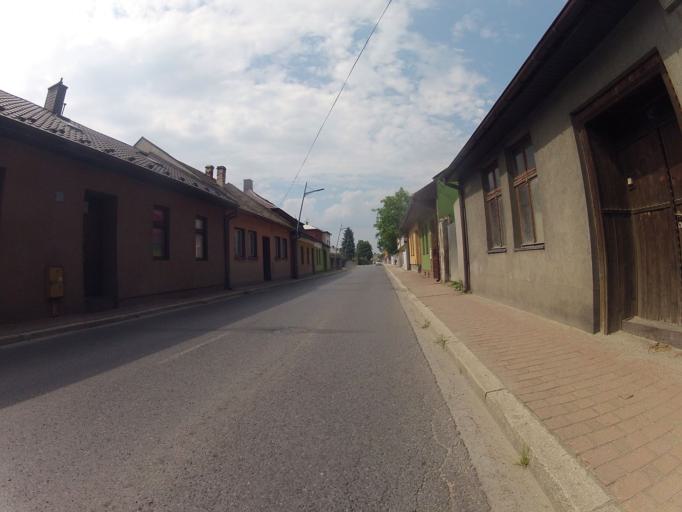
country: PL
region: Lesser Poland Voivodeship
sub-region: Powiat nowosadecki
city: Stary Sacz
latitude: 49.5600
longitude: 20.6371
